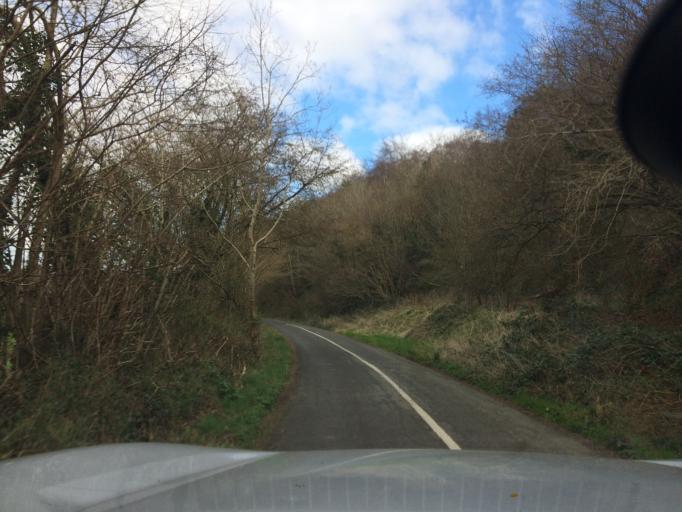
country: IE
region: Munster
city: Carrick-on-Suir
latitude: 52.2844
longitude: -7.3944
